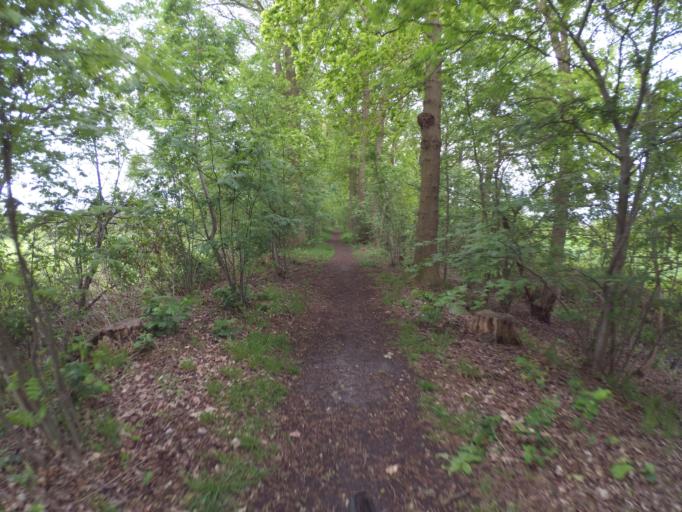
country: NL
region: Utrecht
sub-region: Gemeente Leusden
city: Leusden
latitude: 52.1344
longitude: 5.4573
